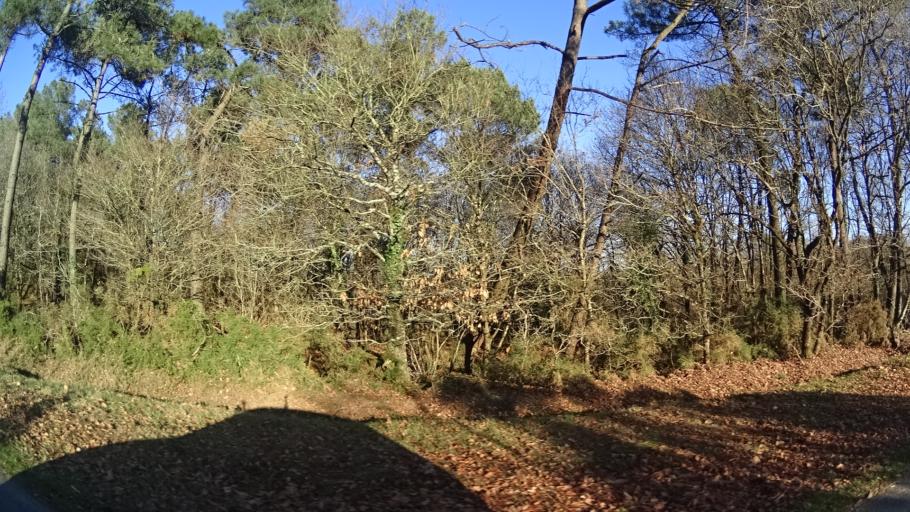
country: FR
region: Brittany
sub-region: Departement du Morbihan
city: Saint-Jacut-les-Pins
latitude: 47.6607
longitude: -2.2064
